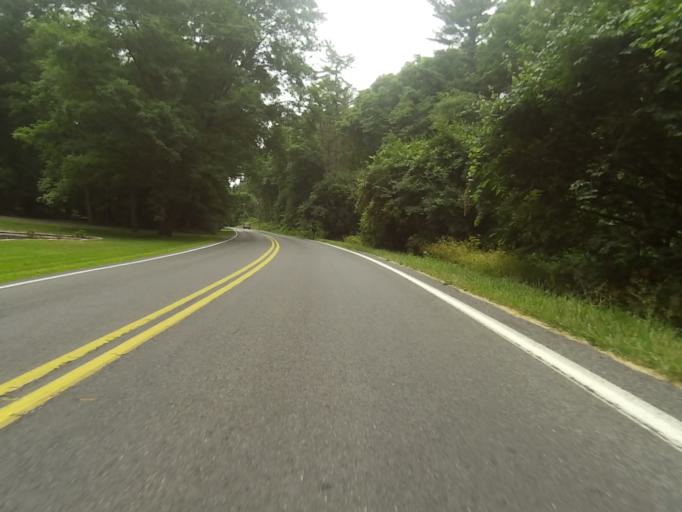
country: US
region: Pennsylvania
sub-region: Centre County
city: Pine Grove Mills
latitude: 40.7416
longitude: -77.9506
